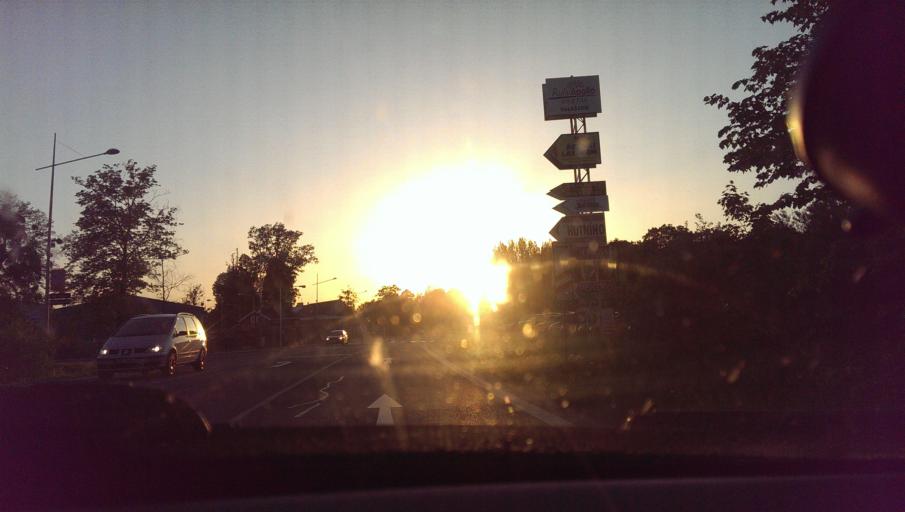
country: CZ
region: Zlin
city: Valasske Mezirici
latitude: 49.4763
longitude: 17.9920
